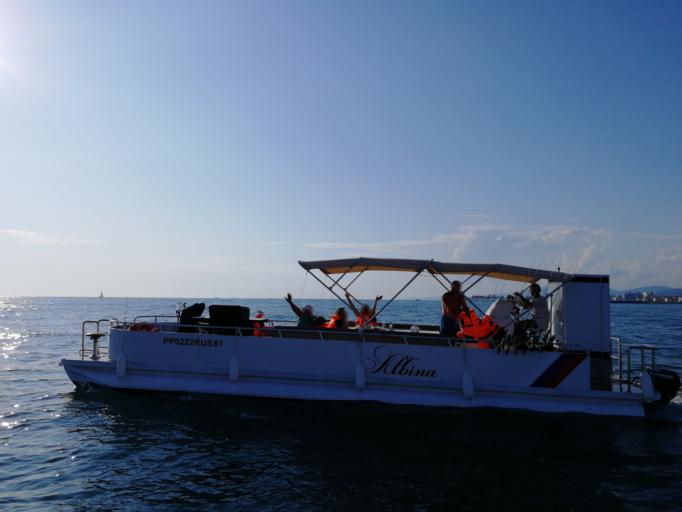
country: RU
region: Krasnodarskiy
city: Adler
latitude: 43.3909
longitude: 39.9468
